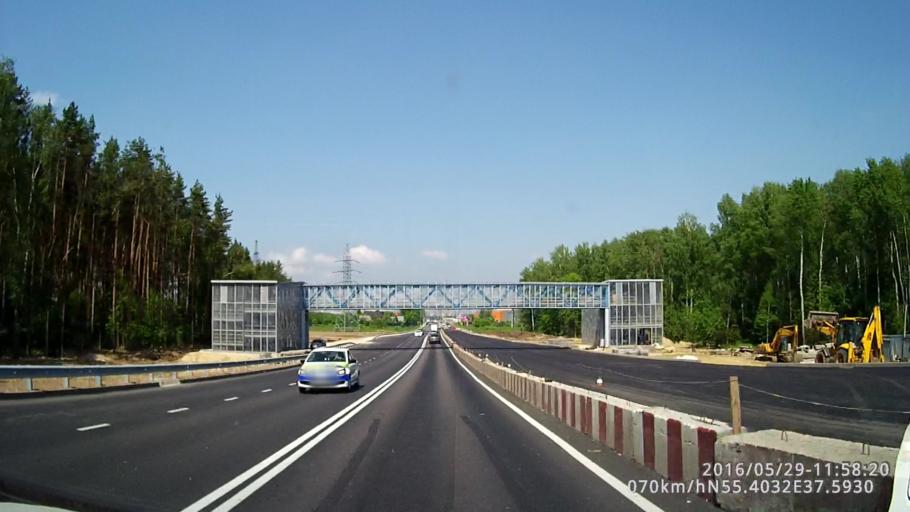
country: RU
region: Moskovskaya
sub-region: Podol'skiy Rayon
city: Podol'sk
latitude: 55.4033
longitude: 37.5922
